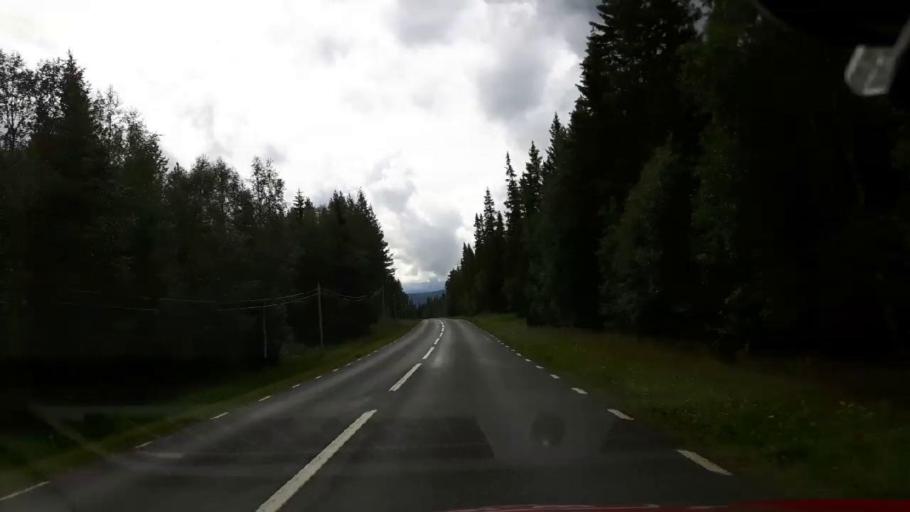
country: NO
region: Nord-Trondelag
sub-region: Lierne
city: Sandvika
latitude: 64.5164
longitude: 14.1597
